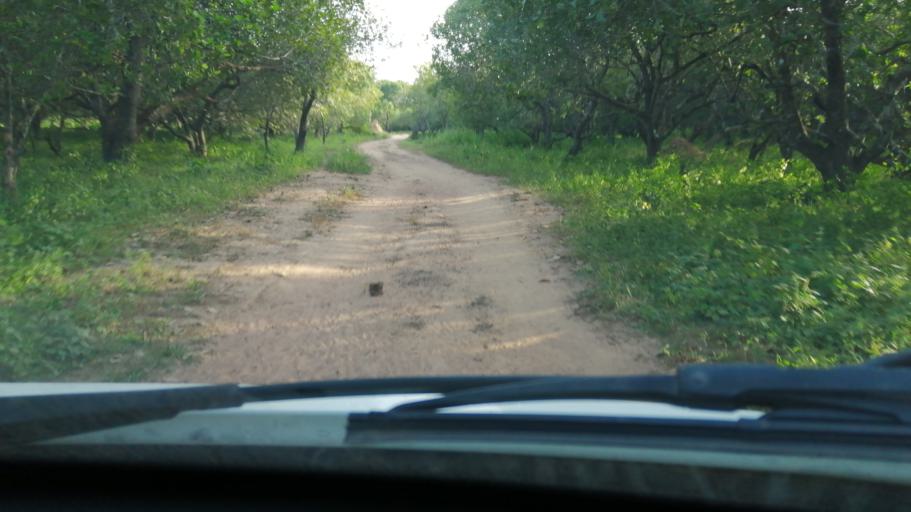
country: GW
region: Oio
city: Mansoa
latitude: 11.9998
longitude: -15.4720
